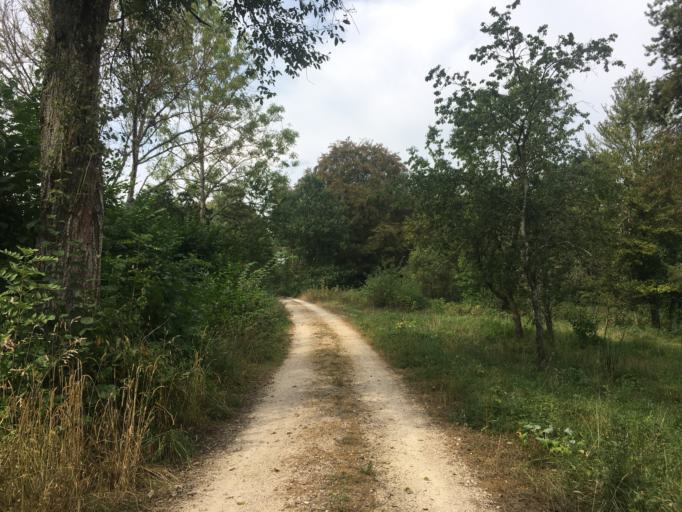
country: DE
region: Baden-Wuerttemberg
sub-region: Tuebingen Region
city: Hayingen
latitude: 48.2807
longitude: 9.4949
